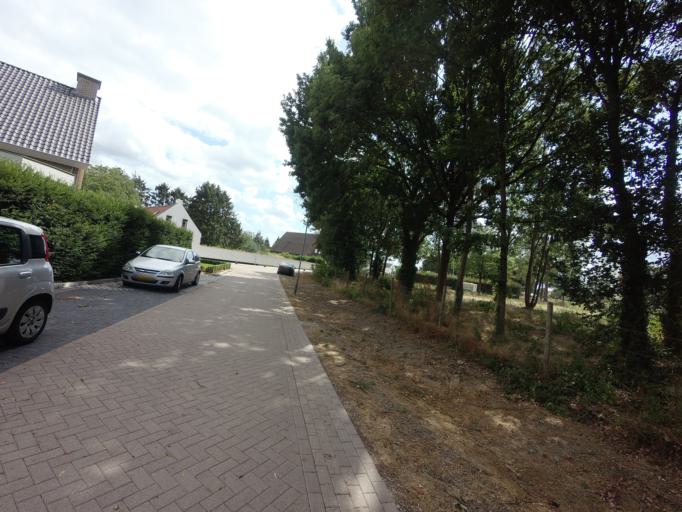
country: NL
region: Limburg
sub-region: Gemeente Maasgouw
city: Maasbracht
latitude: 51.1369
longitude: 5.8617
